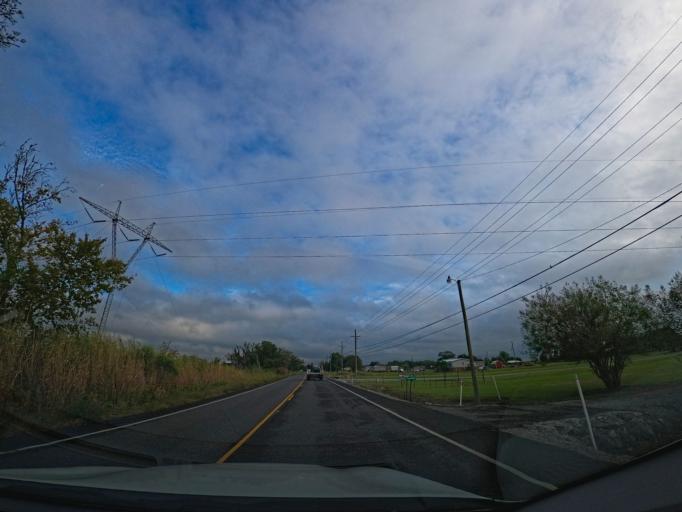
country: US
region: Louisiana
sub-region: Terrebonne Parish
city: Dulac
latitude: 29.4487
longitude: -90.7025
